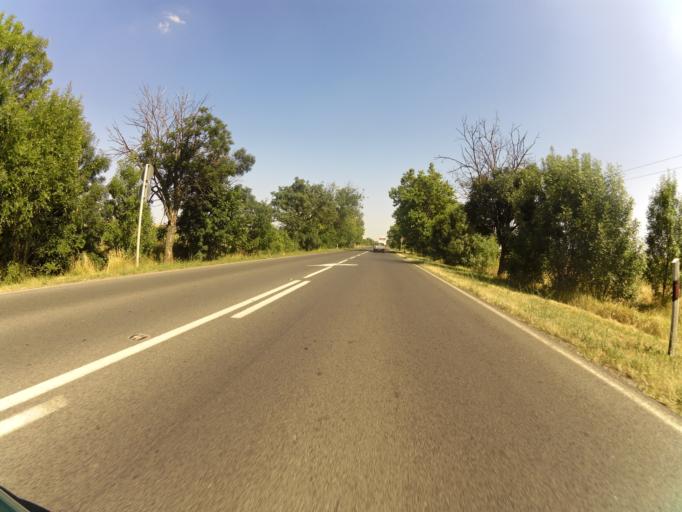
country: HU
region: Csongrad
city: Szatymaz
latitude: 46.3000
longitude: 20.0743
